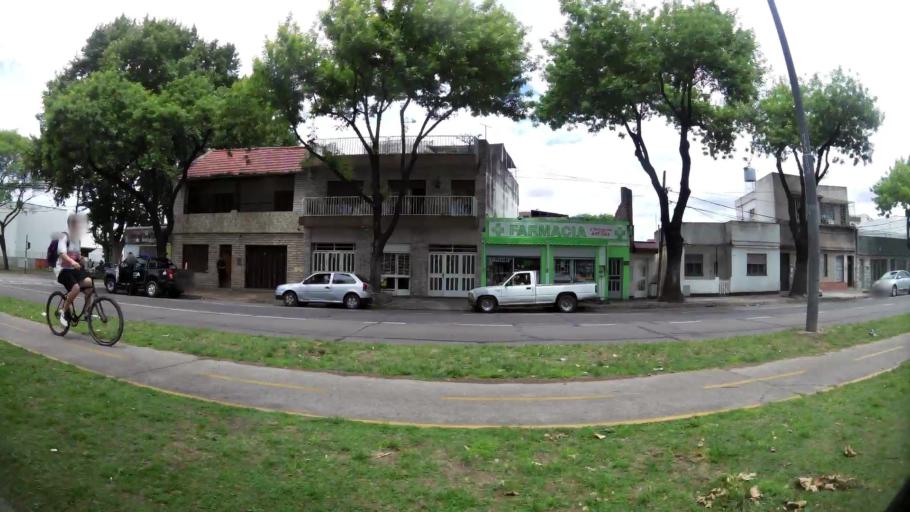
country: AR
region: Santa Fe
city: Gobernador Galvez
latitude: -32.9906
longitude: -60.6441
